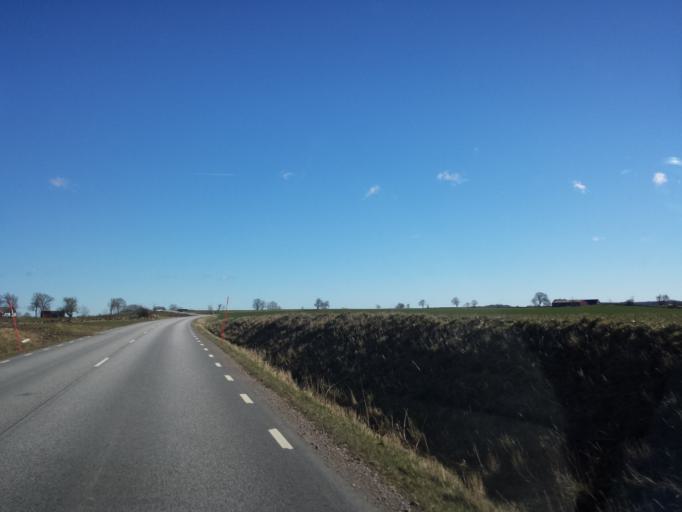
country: SE
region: Skane
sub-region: Tomelilla Kommun
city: Tomelilla
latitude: 55.6324
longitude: 13.8695
